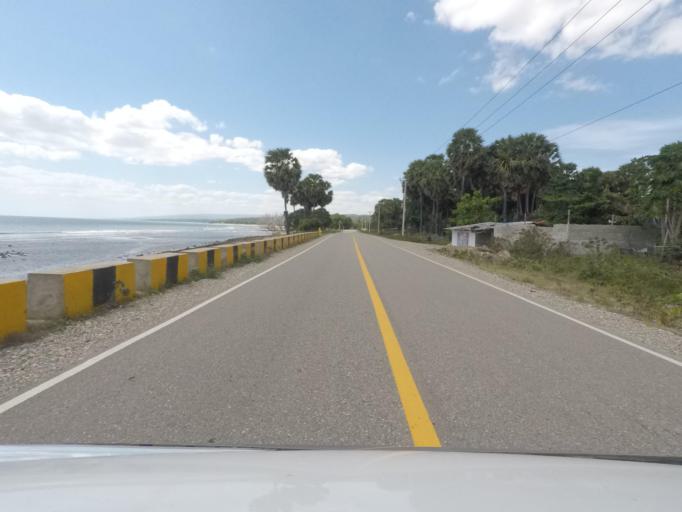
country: TL
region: Lautem
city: Lospalos
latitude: -8.4214
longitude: 126.7604
